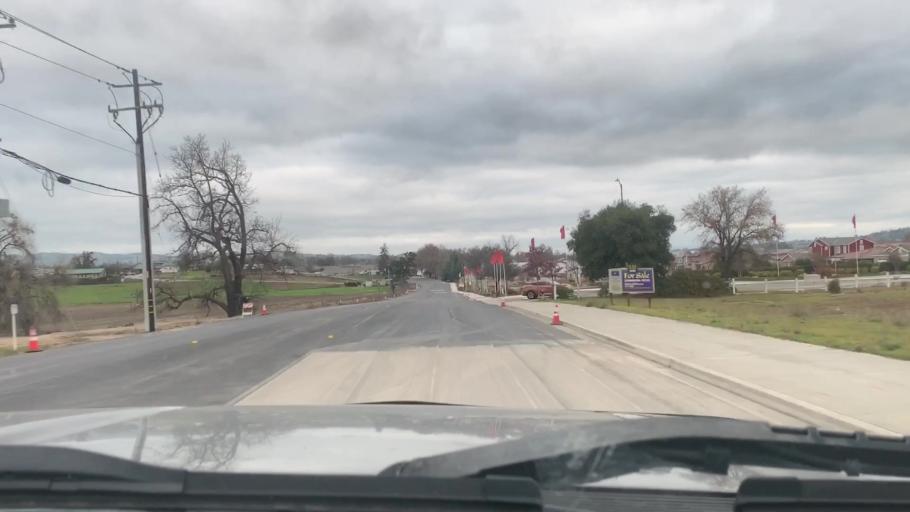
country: US
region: California
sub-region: San Luis Obispo County
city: Templeton
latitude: 35.5589
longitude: -120.7009
